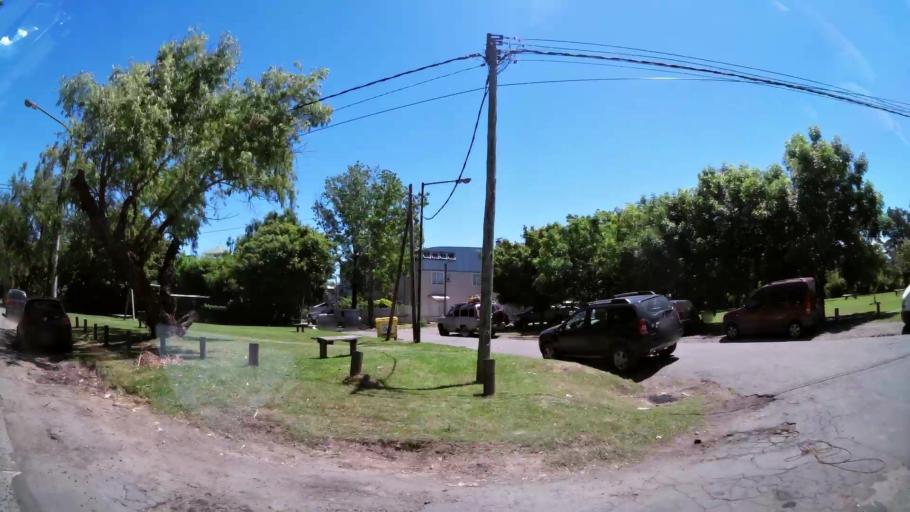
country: AR
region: Buenos Aires
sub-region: Partido de San Isidro
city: San Isidro
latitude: -34.4595
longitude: -58.5065
